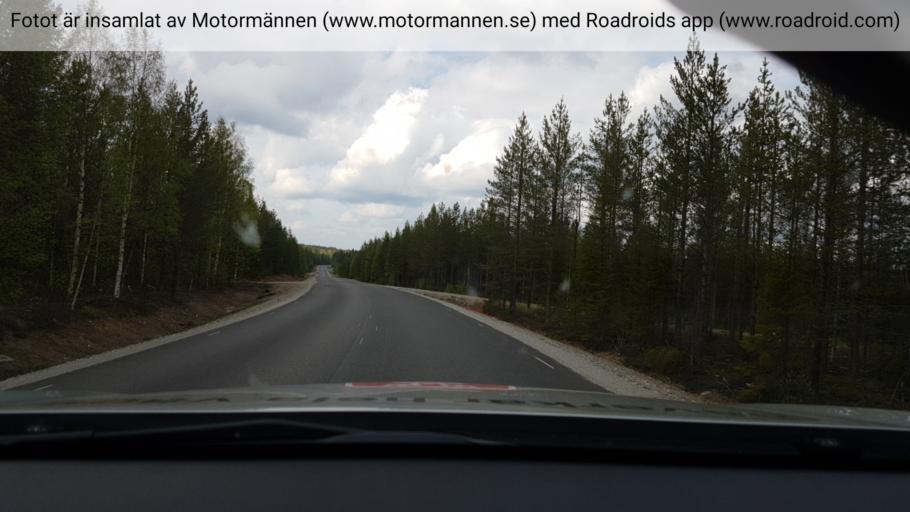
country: SE
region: Vaesterbotten
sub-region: Lycksele Kommun
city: Lycksele
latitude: 64.0560
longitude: 18.4185
